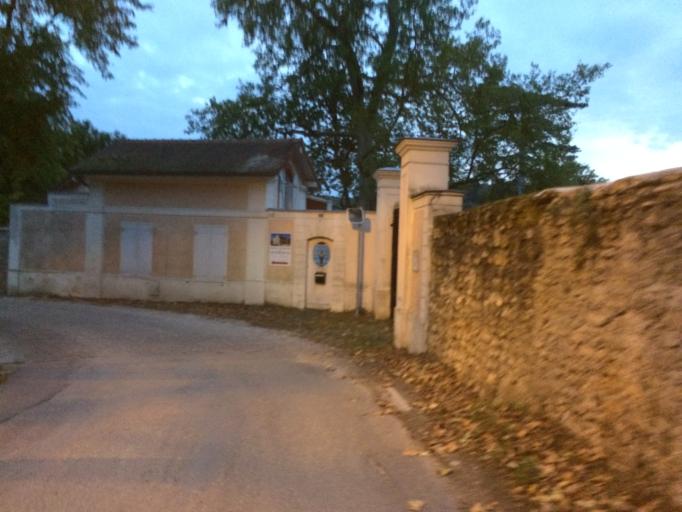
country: FR
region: Ile-de-France
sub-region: Departement de l'Essonne
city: Bievres
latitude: 48.7571
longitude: 2.2017
